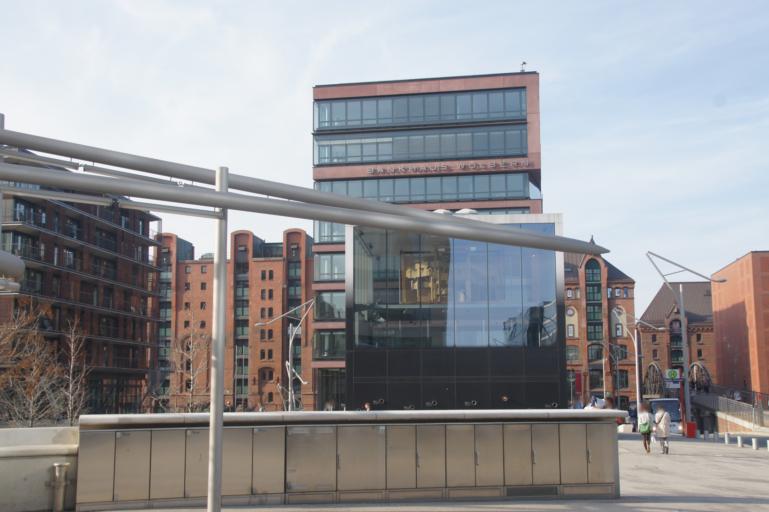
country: DE
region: Hamburg
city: Altstadt
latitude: 53.5421
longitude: 9.9929
